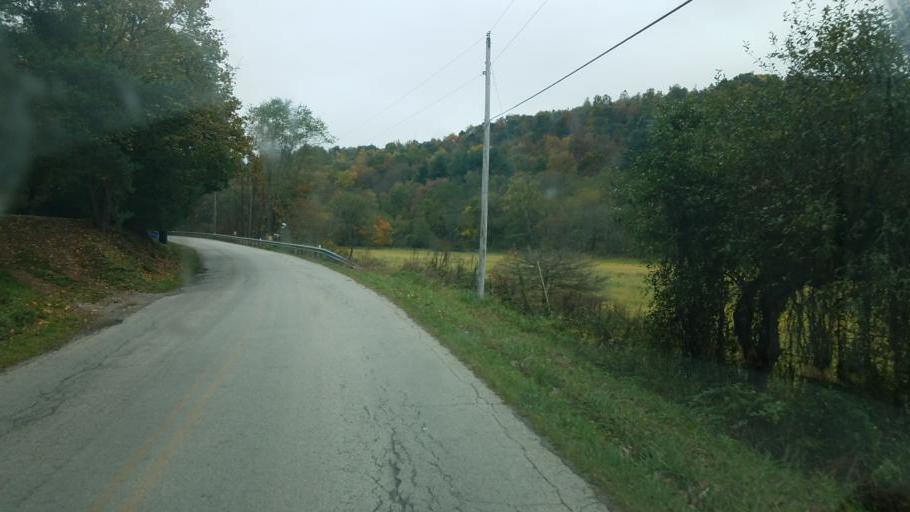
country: US
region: Ohio
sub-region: Ashland County
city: Loudonville
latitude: 40.5272
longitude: -82.1030
